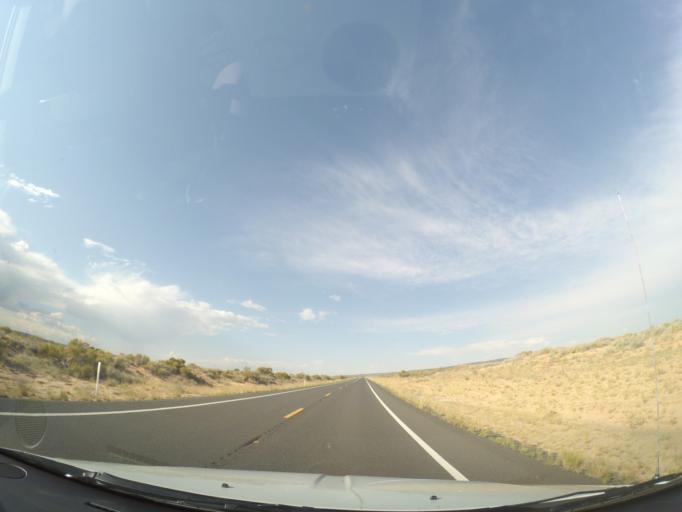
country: US
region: Arizona
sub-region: Coconino County
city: Tuba City
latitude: 36.4571
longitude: -111.4239
